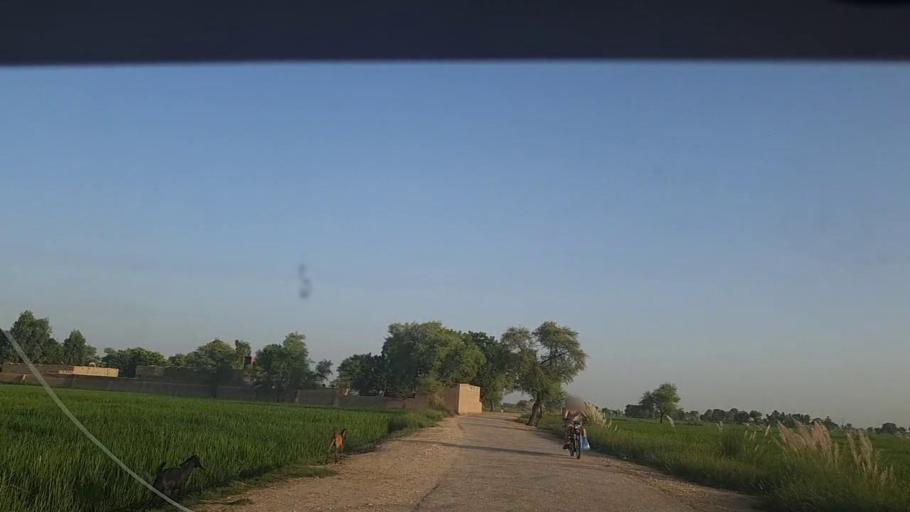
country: PK
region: Sindh
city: Thul
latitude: 28.1294
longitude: 68.8921
